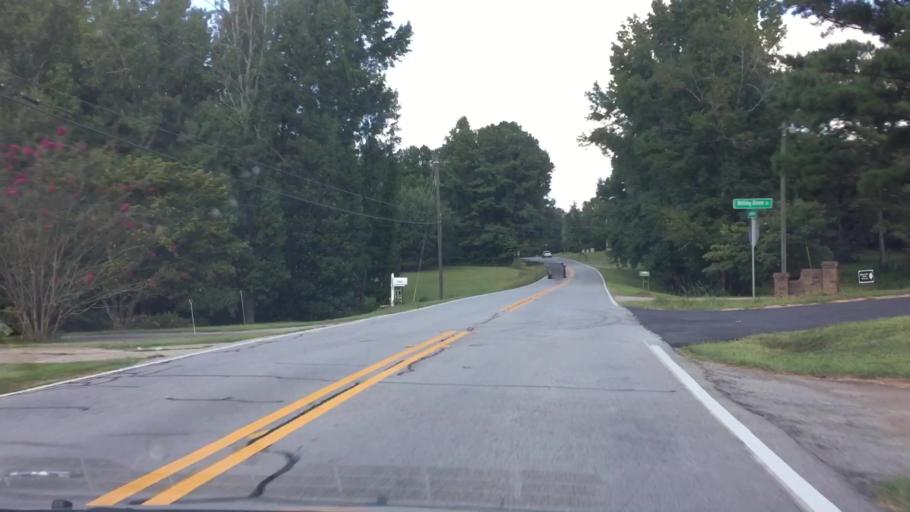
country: US
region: Georgia
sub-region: Fayette County
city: Shannon
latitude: 33.4135
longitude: -84.4829
